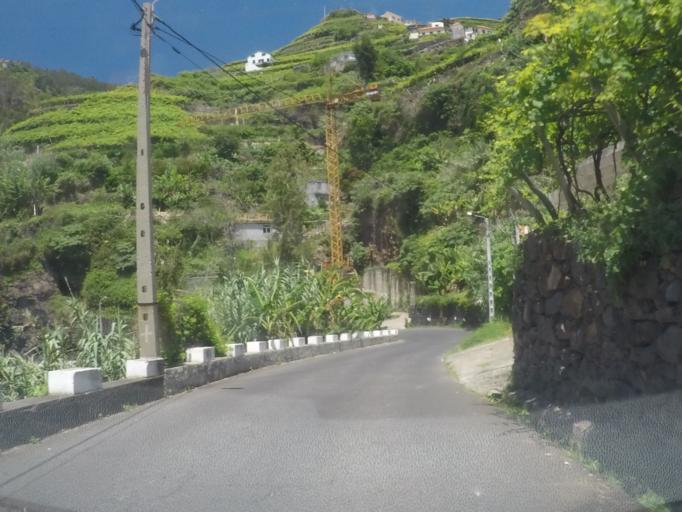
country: PT
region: Madeira
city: Camara de Lobos
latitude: 32.6720
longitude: -16.9854
